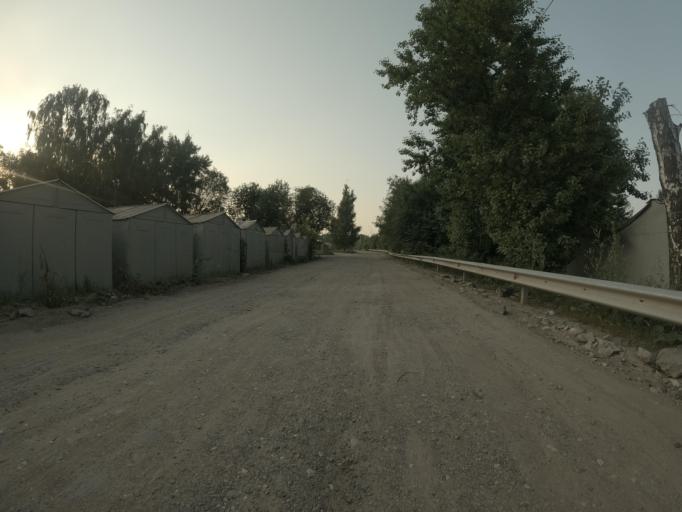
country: RU
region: St.-Petersburg
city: Krasnogvargeisky
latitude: 59.9558
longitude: 30.4566
